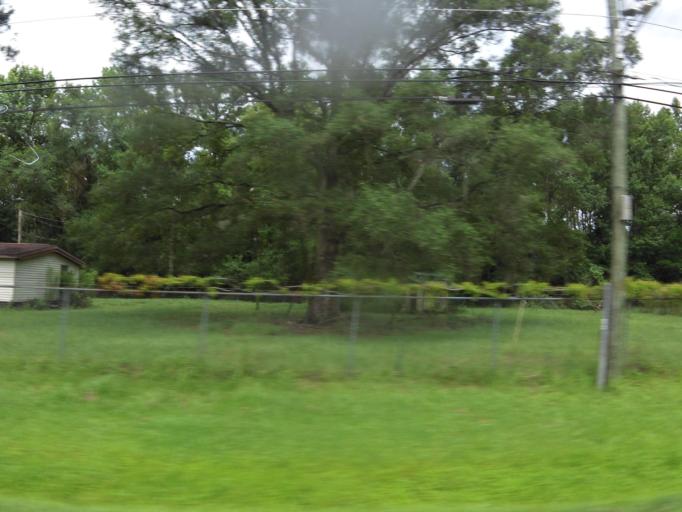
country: US
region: Florida
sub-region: Nassau County
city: Nassau Village-Ratliff
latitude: 30.4417
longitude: -81.7728
